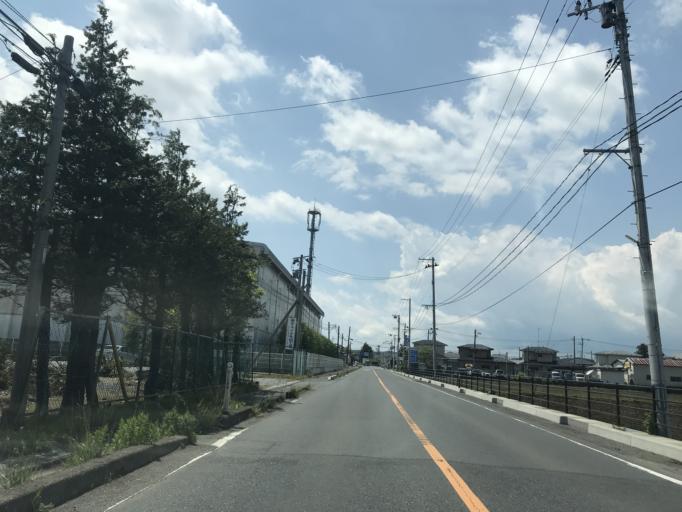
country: JP
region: Miyagi
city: Kogota
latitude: 38.5358
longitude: 141.0549
